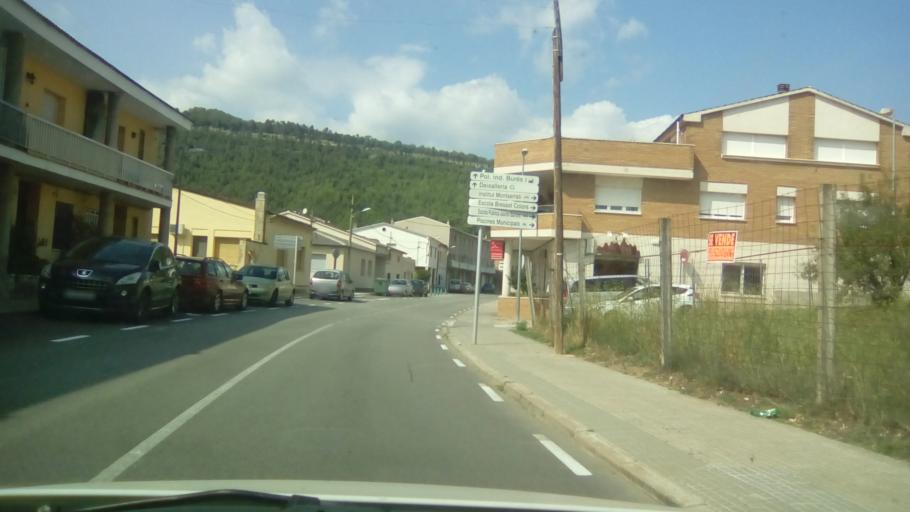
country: ES
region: Catalonia
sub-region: Provincia de Barcelona
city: Monistrol de Montserrat
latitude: 41.6305
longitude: 1.8559
